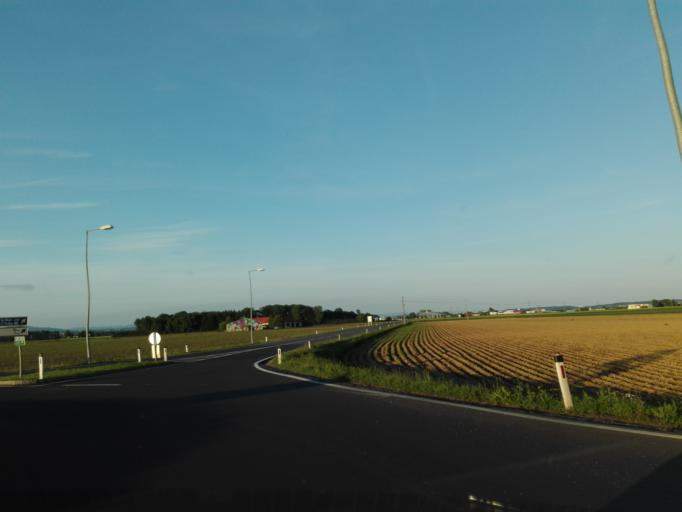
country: AT
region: Upper Austria
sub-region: Politischer Bezirk Linz-Land
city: Pasching
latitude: 48.2423
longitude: 14.2042
